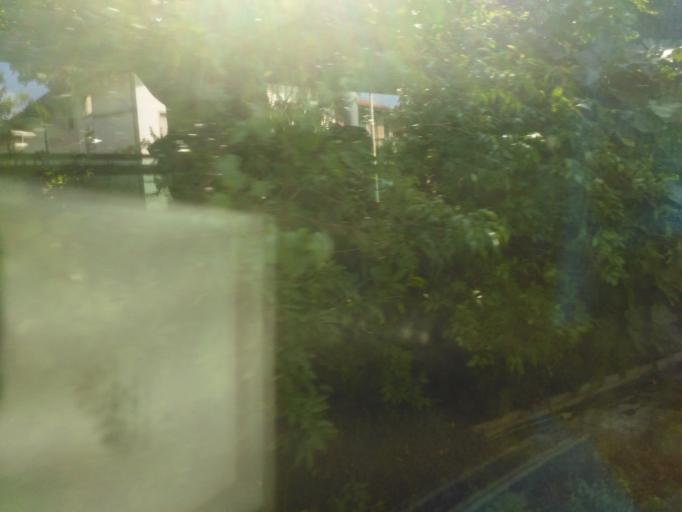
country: IT
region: Lombardy
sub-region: Provincia di Bergamo
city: Romano di Lombardia
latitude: 45.5239
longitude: 9.7563
